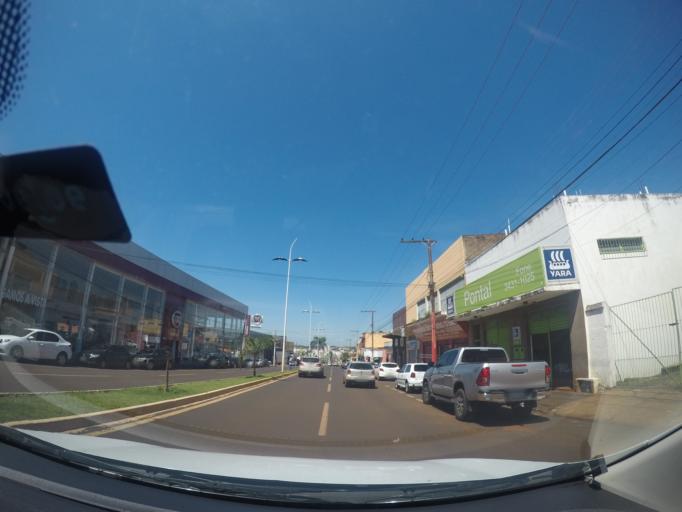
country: BR
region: Goias
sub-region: Itumbiara
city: Itumbiara
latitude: -18.4076
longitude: -49.2117
